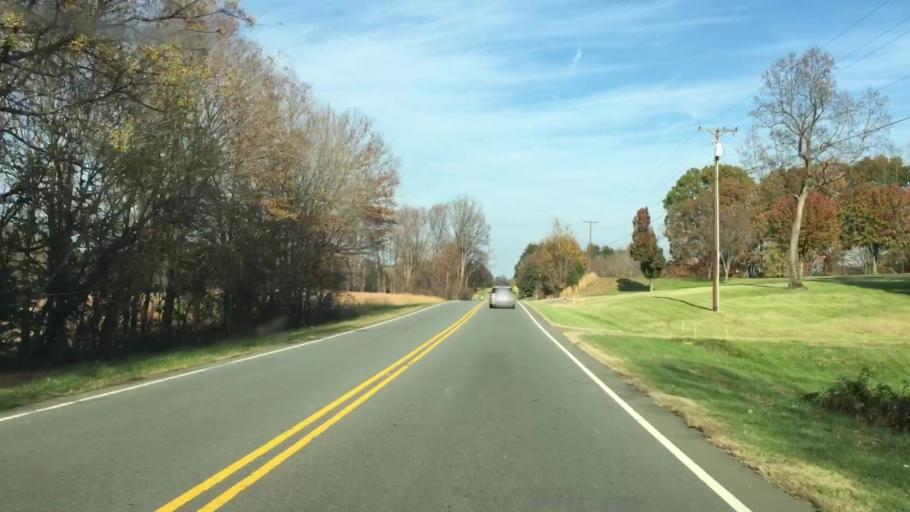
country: US
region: North Carolina
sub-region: Forsyth County
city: Walkertown
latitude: 36.1747
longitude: -80.1266
